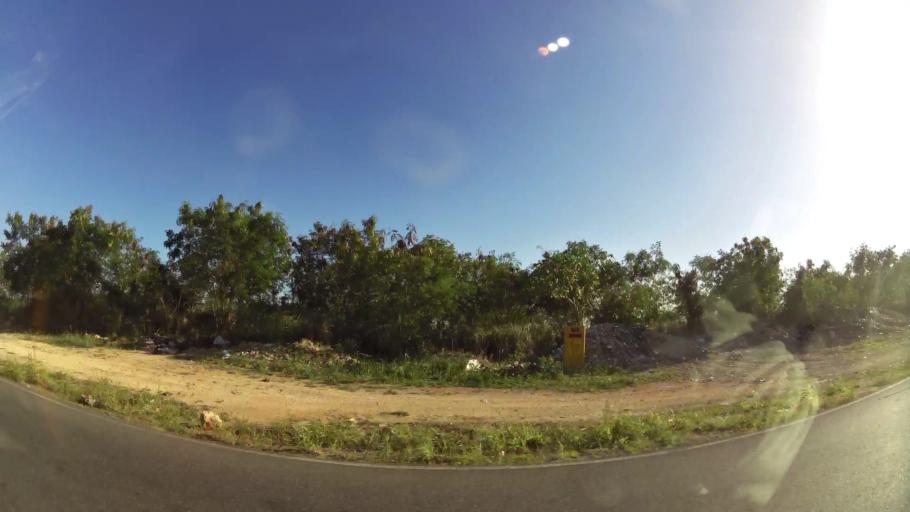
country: DO
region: Santo Domingo
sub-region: Santo Domingo
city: Santo Domingo Este
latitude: 18.4836
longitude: -69.8146
